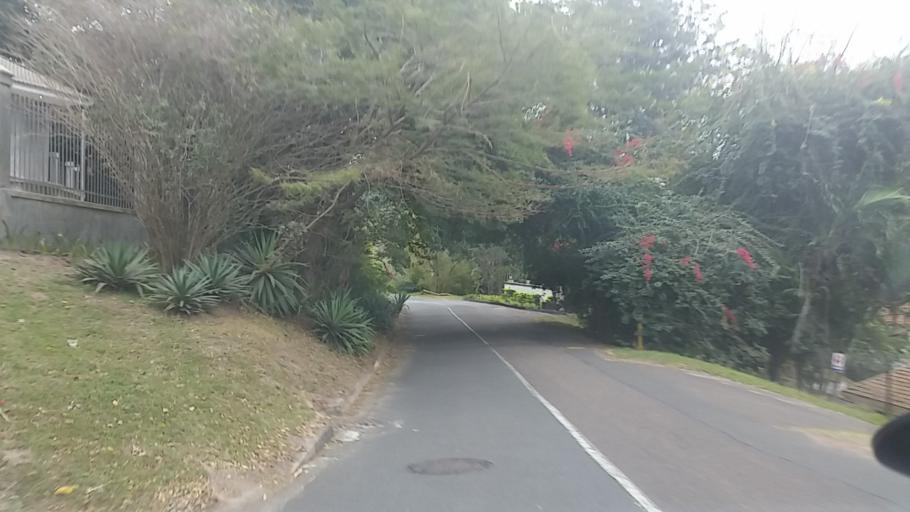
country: ZA
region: KwaZulu-Natal
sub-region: eThekwini Metropolitan Municipality
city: Berea
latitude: -29.8412
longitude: 30.9324
